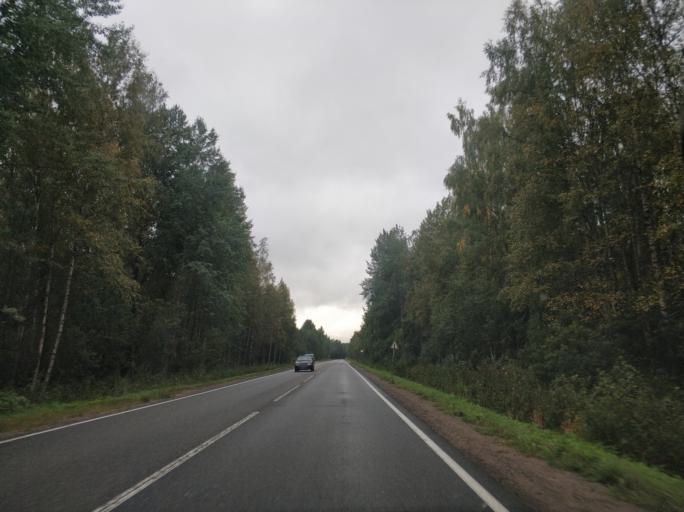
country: RU
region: Leningrad
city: Borisova Griva
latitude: 60.1202
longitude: 30.9635
